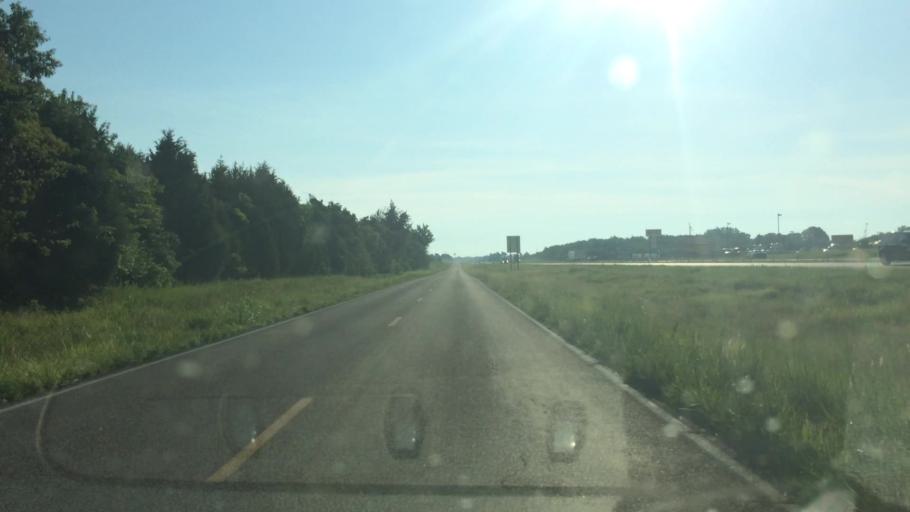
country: US
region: Missouri
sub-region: Greene County
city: Strafford
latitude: 37.2565
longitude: -93.1657
